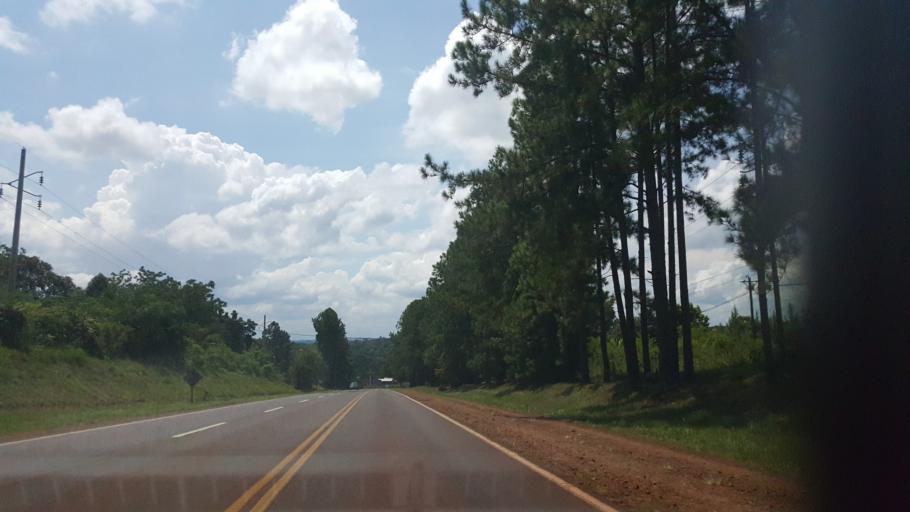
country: AR
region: Misiones
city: Puerto Rico
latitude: -26.8370
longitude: -55.0381
